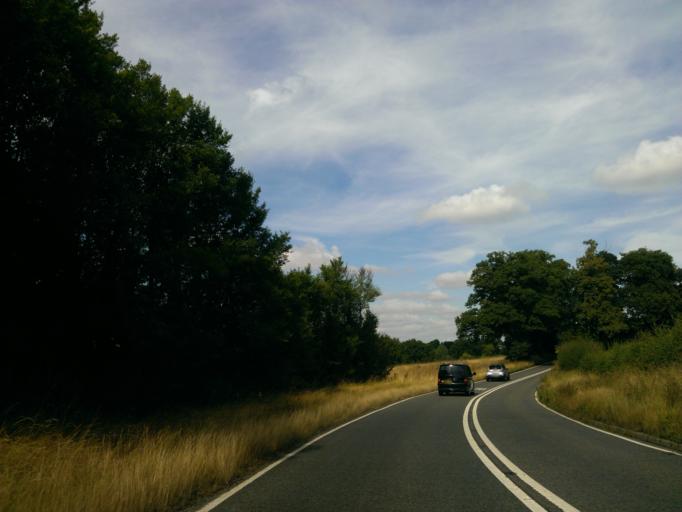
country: GB
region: England
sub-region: Essex
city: Sible Hedingham
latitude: 51.9552
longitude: 0.6306
